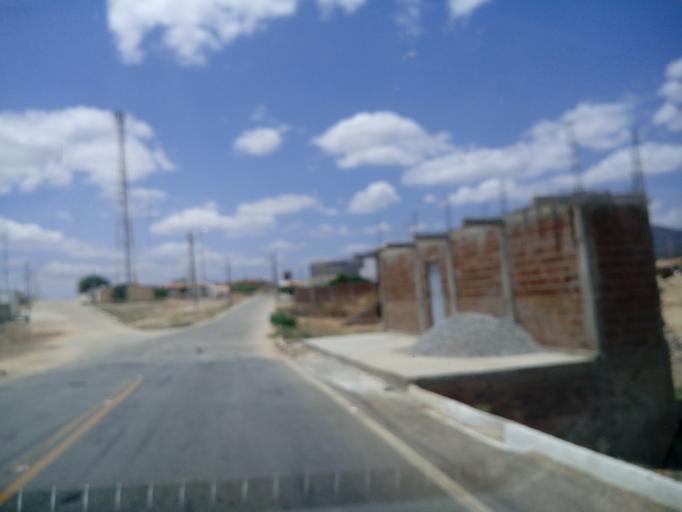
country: BR
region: Paraiba
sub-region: Patos
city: Patos
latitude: -7.0312
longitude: -37.1510
